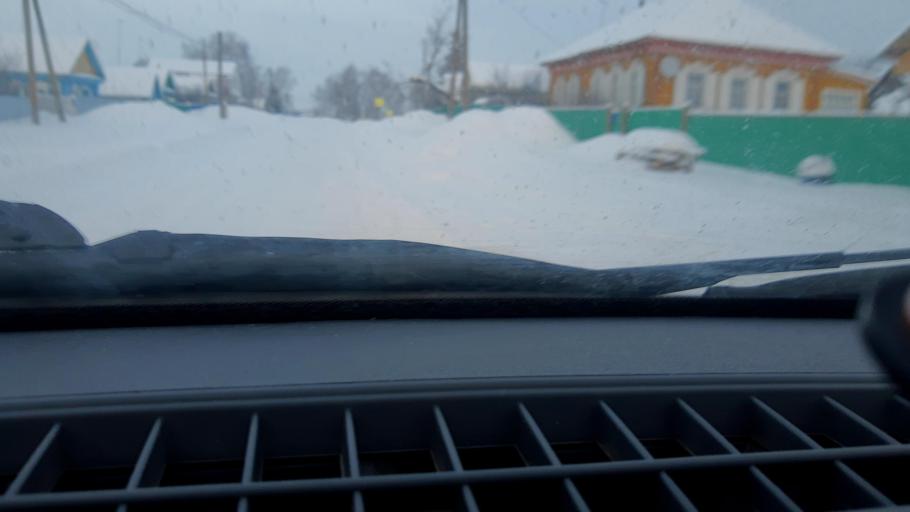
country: RU
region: Bashkortostan
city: Davlekanovo
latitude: 54.5386
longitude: 55.0456
